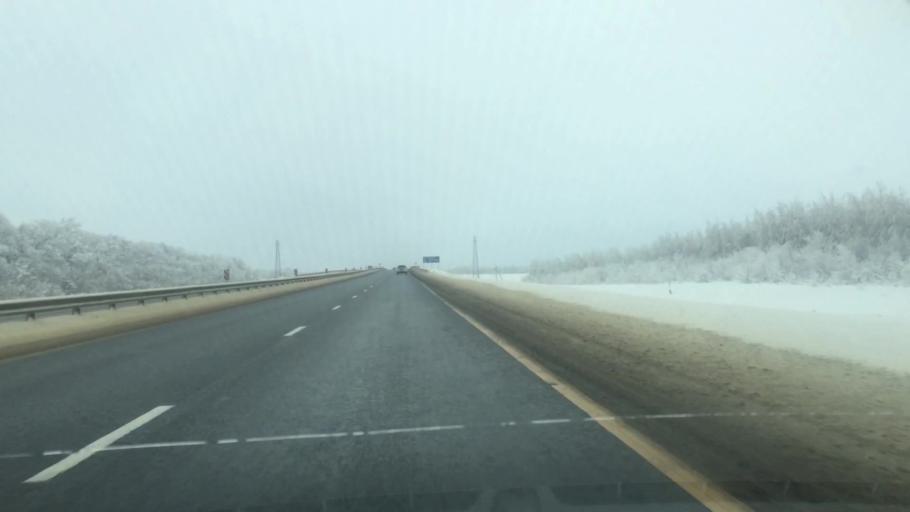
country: RU
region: Lipetsk
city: Zadonsk
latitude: 52.5089
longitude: 38.7557
